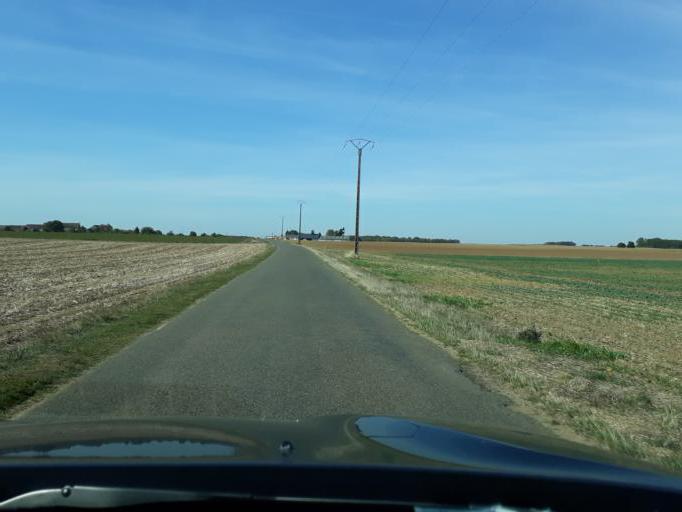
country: FR
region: Centre
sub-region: Departement du Loir-et-Cher
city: Ouzouer-le-Marche
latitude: 47.9417
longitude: 1.5337
